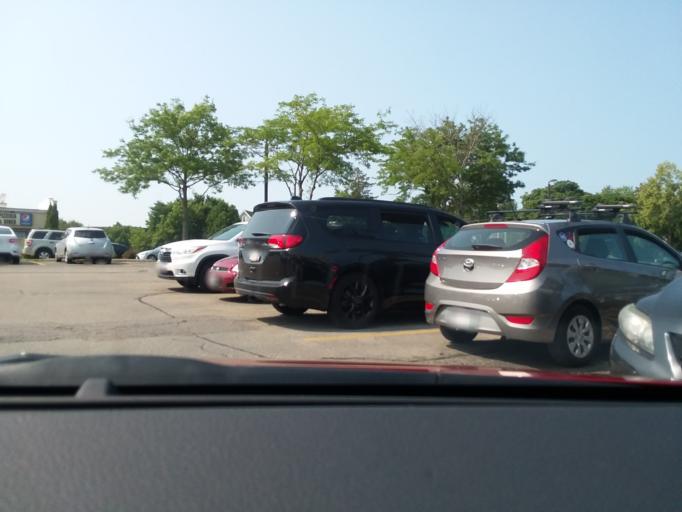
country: US
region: Wisconsin
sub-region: Dane County
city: Verona
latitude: 42.9886
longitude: -89.5339
